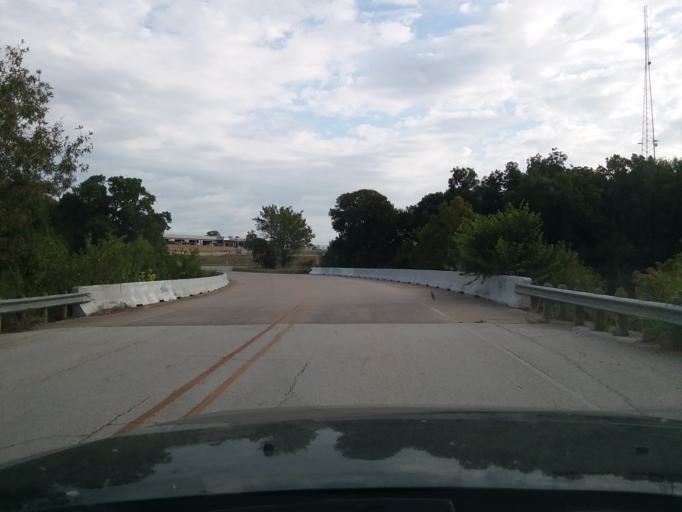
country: US
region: Texas
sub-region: Denton County
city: Copper Canyon
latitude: 33.1293
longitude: -97.1046
